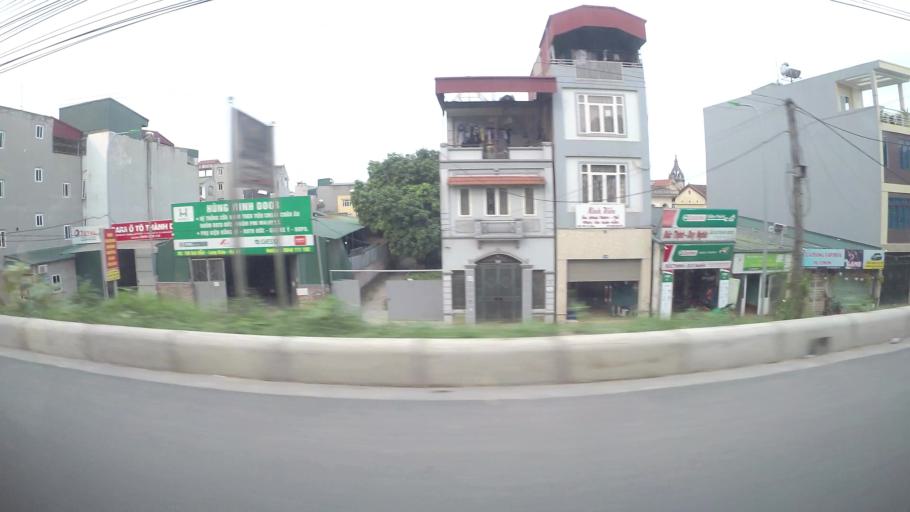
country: VN
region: Ha Noi
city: Hoan Kiem
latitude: 21.0252
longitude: 105.8846
